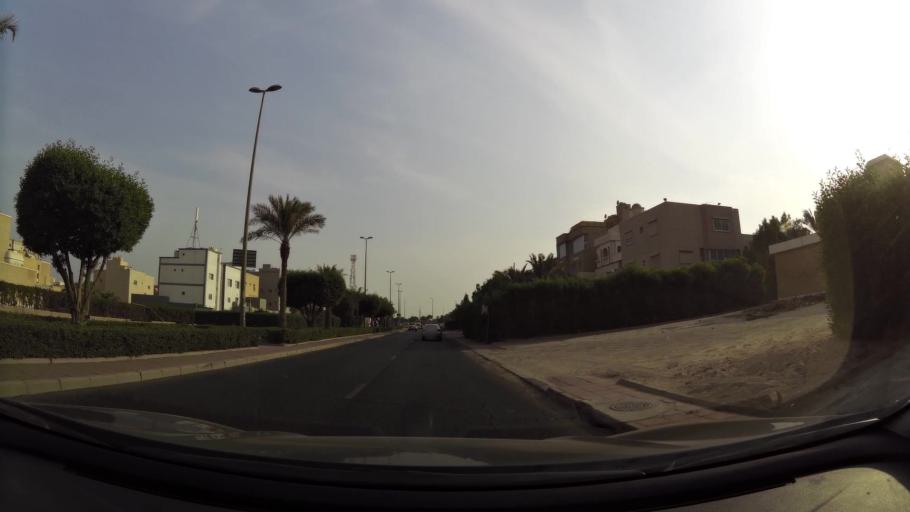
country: KW
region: Mubarak al Kabir
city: Sabah as Salim
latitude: 29.2393
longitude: 48.0614
